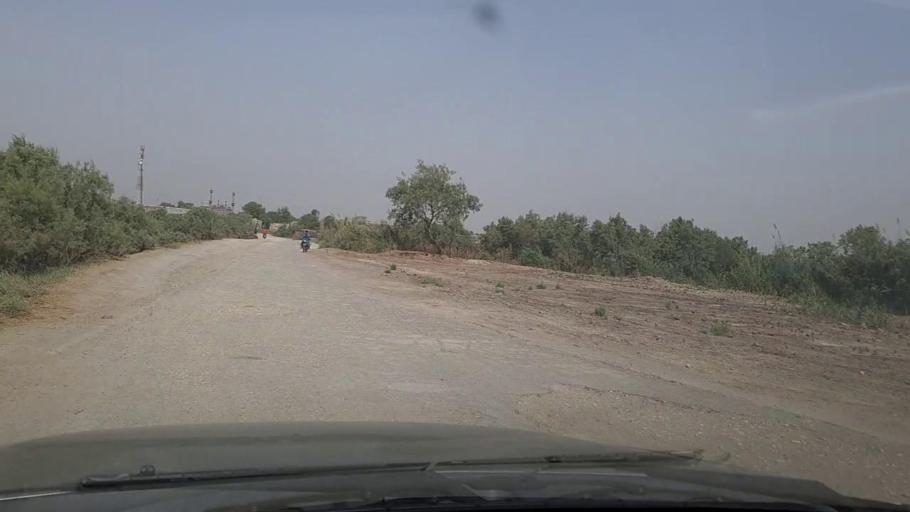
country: PK
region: Balochistan
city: Sohbatpur
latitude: 28.4237
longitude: 68.6760
